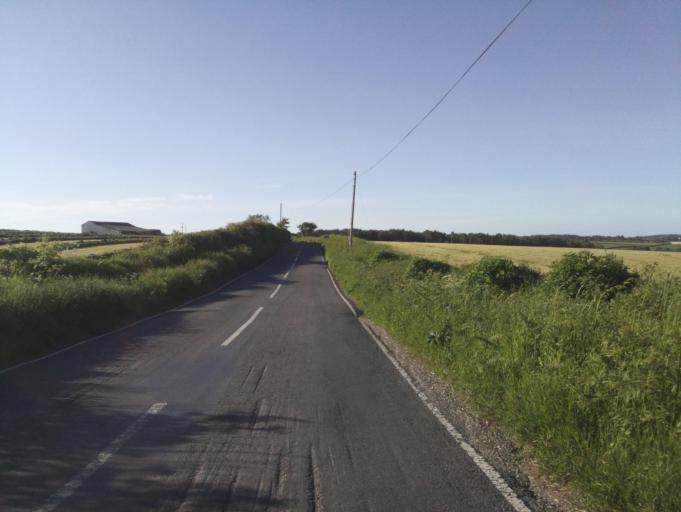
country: GB
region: England
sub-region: Dorset
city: Lyme Regis
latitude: 50.7187
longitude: -2.9889
